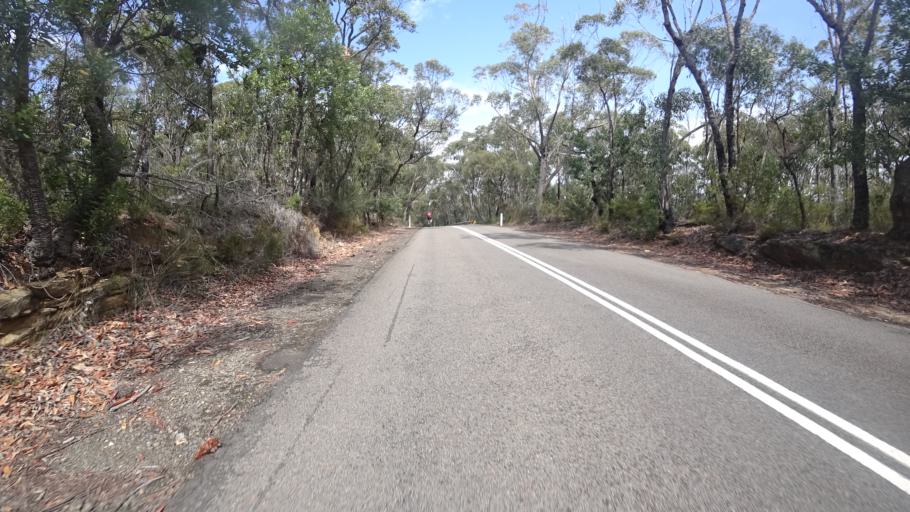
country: AU
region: New South Wales
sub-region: Hornsby Shire
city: Mount Colah
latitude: -33.6730
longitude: 151.1402
